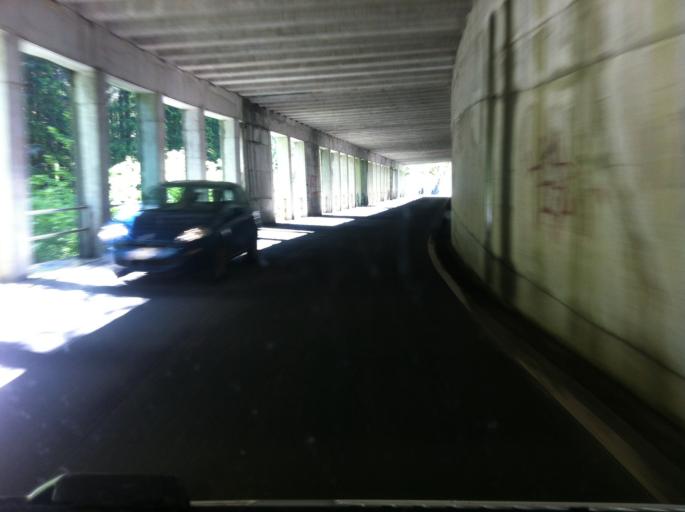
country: IT
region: Lombardy
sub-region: Provincia di Sondrio
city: Campodolcino
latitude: 46.4274
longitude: 9.3398
